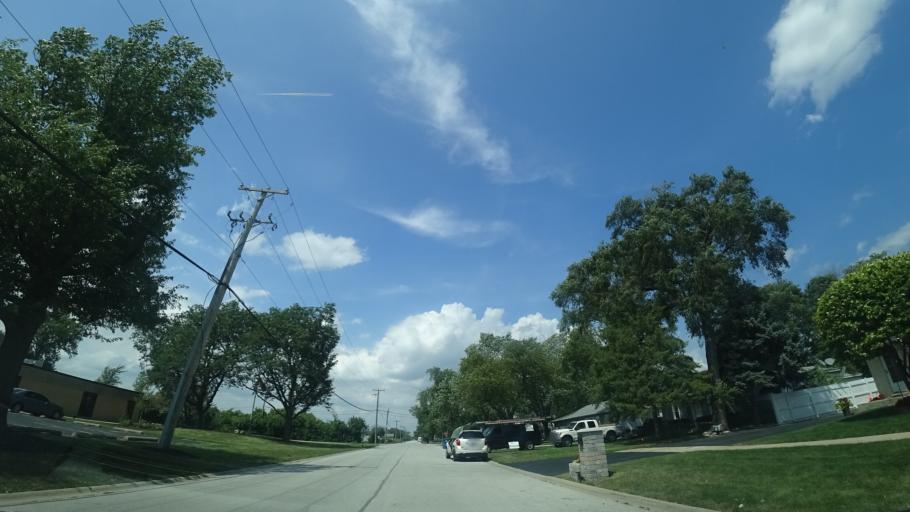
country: US
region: Illinois
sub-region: Cook County
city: Alsip
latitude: 41.6754
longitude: -87.7490
